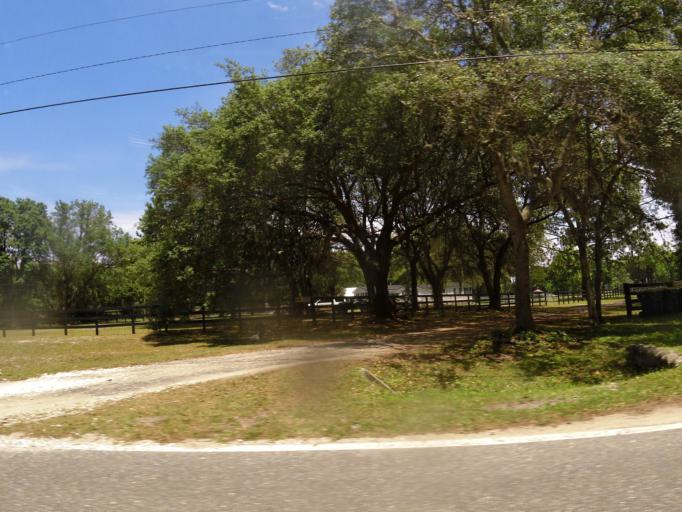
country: US
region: Florida
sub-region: Duval County
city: Atlantic Beach
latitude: 30.4572
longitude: -81.4683
